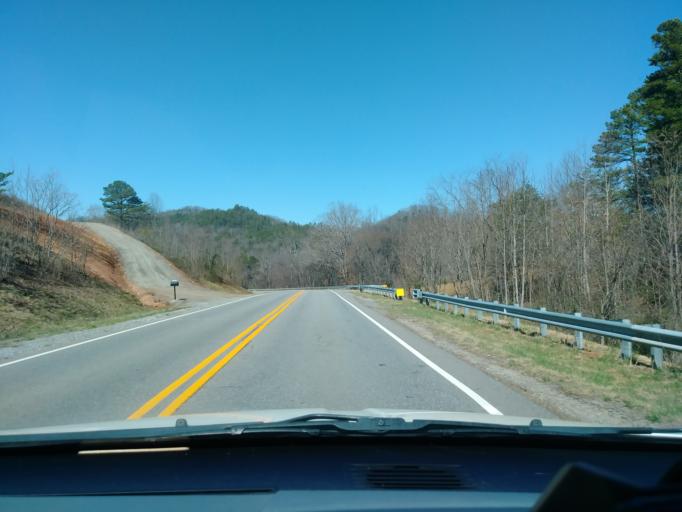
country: US
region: North Carolina
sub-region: Madison County
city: Marshall
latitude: 35.9037
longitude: -82.8676
